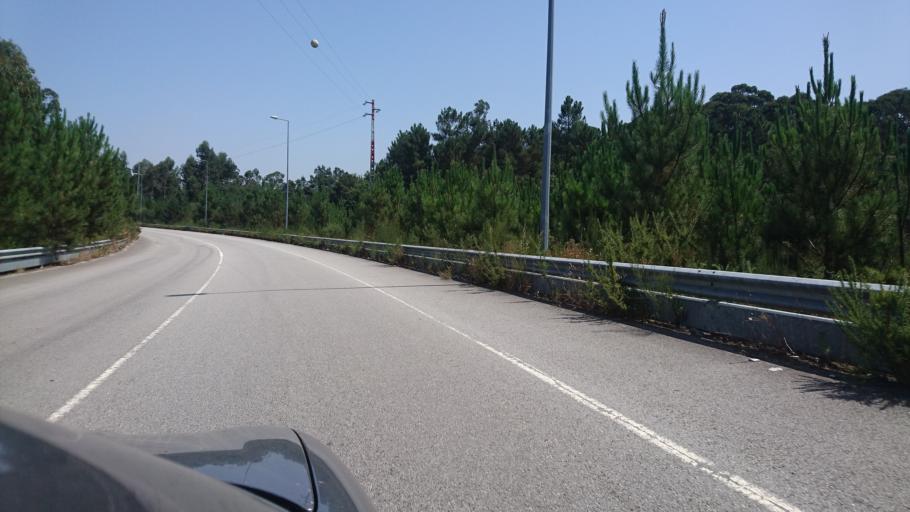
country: PT
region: Porto
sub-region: Valongo
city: Campo
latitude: 41.1670
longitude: -8.4410
